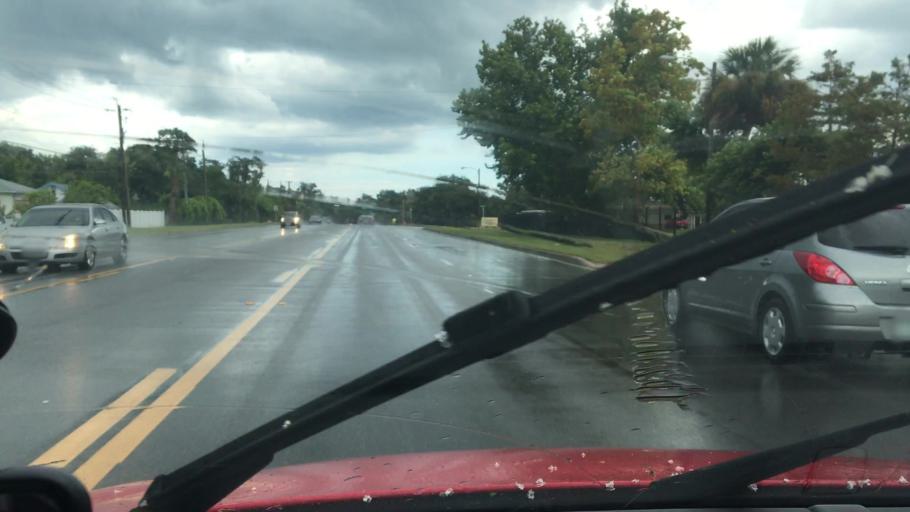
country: US
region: Florida
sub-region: Volusia County
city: Daytona Beach
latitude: 29.2089
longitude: -81.0526
